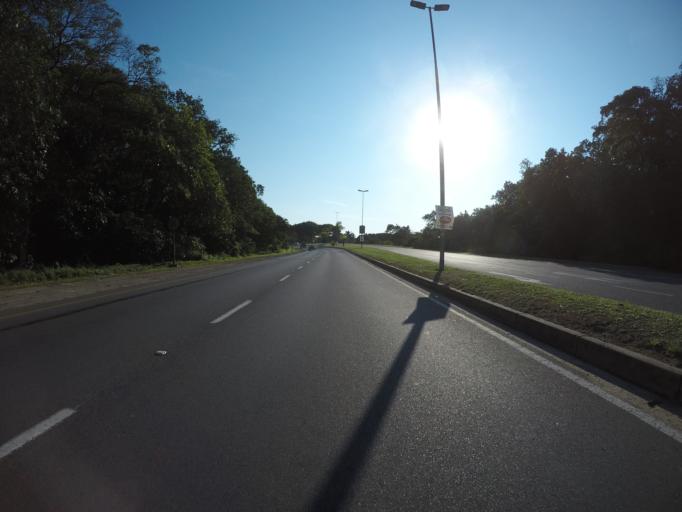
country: ZA
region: KwaZulu-Natal
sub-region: uThungulu District Municipality
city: Richards Bay
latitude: -28.7686
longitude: 32.0596
